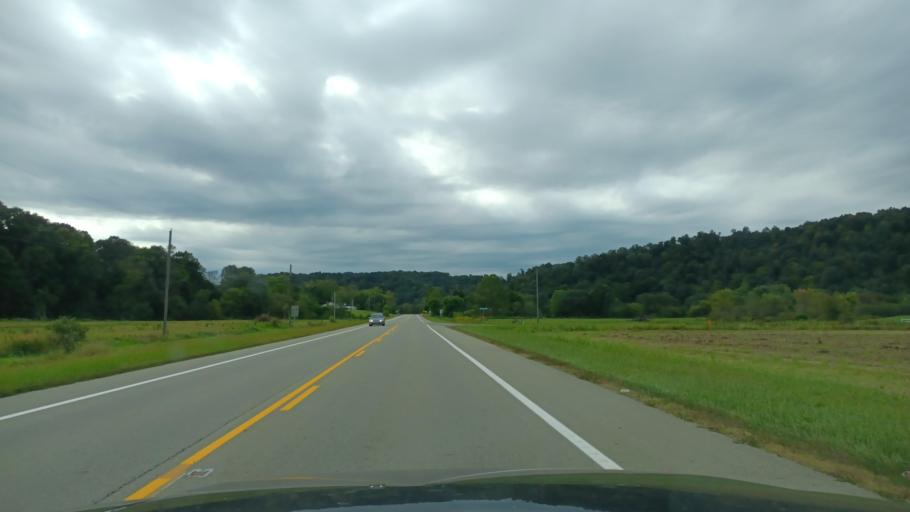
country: US
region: Ohio
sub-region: Vinton County
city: McArthur
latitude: 39.2750
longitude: -82.6213
